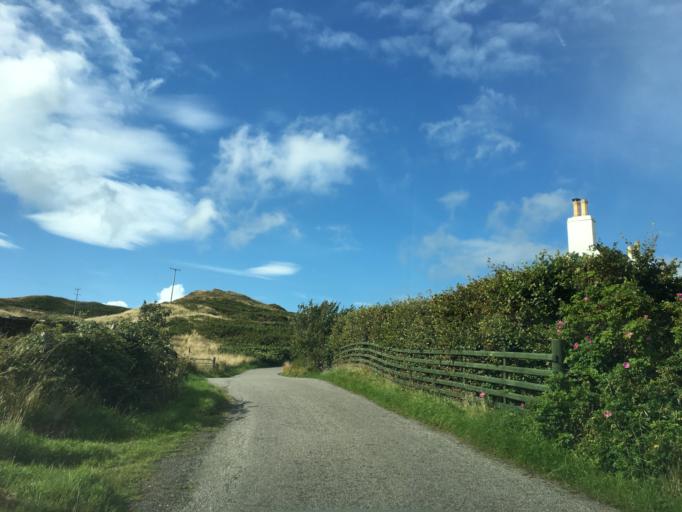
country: GB
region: Scotland
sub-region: Argyll and Bute
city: Oban
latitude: 56.2723
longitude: -5.6266
